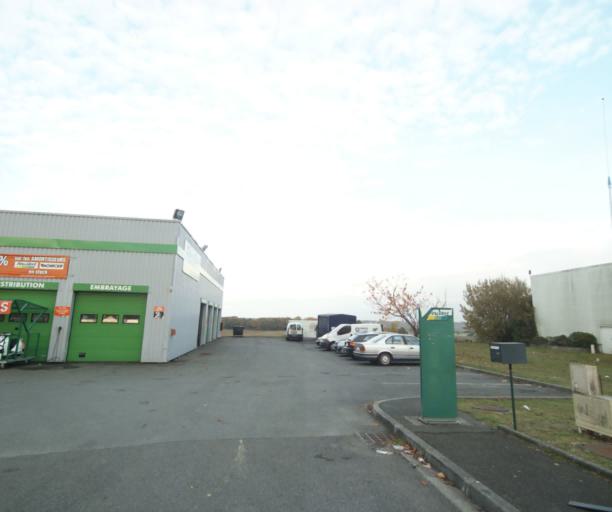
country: FR
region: Poitou-Charentes
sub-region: Departement de la Charente-Maritime
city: Saintes
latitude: 45.7563
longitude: -0.6511
